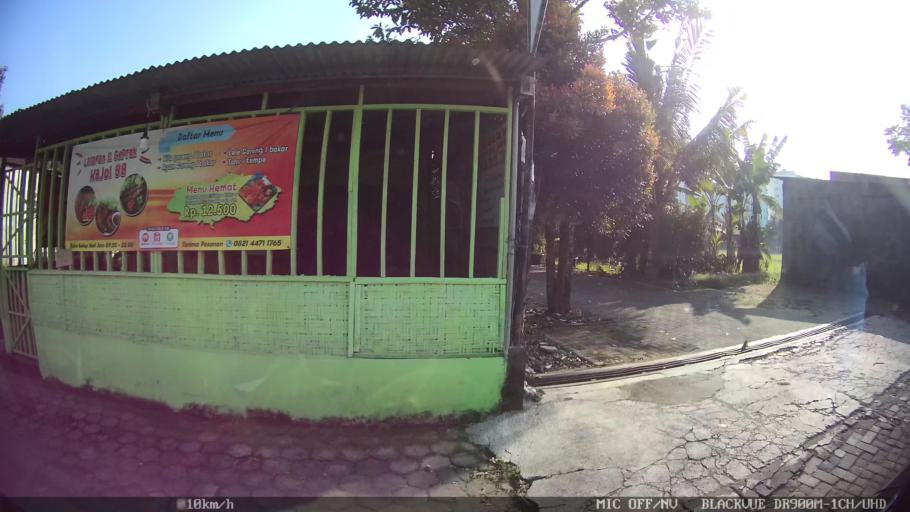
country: ID
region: Daerah Istimewa Yogyakarta
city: Depok
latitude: -7.7742
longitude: 110.4058
